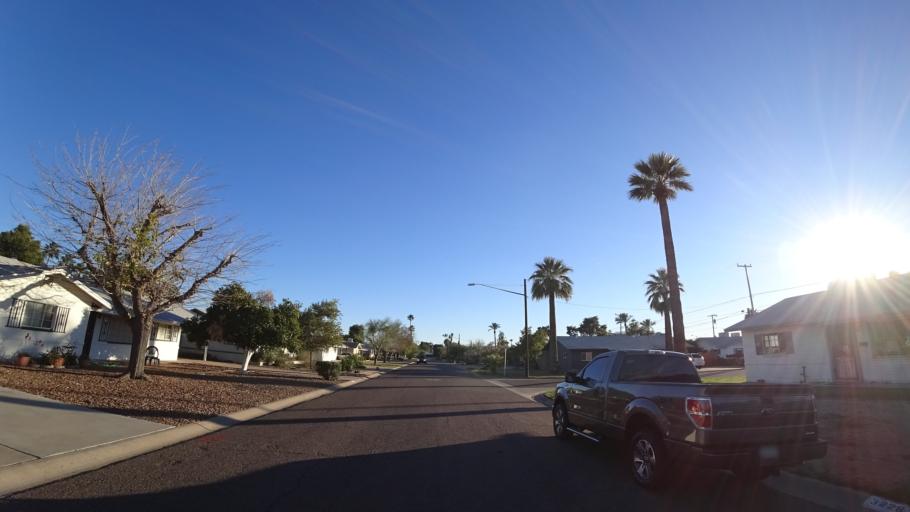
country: US
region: Arizona
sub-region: Maricopa County
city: Phoenix
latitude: 33.4863
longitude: -112.0365
